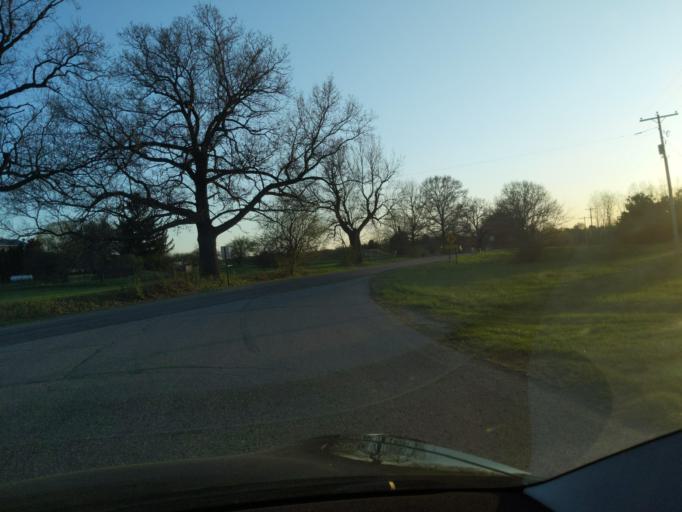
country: US
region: Michigan
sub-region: Ingham County
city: Stockbridge
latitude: 42.4901
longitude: -84.2923
